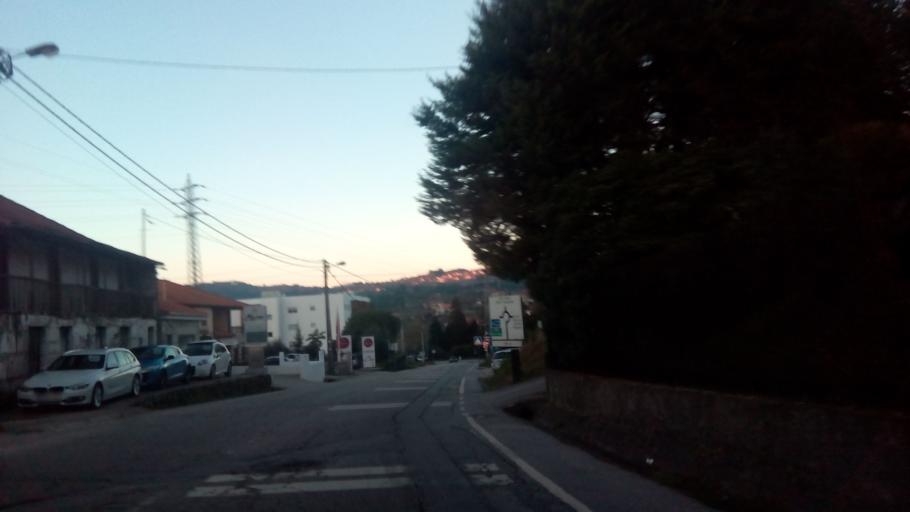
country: PT
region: Porto
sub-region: Amarante
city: Teloes
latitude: 41.2912
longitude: -8.0979
